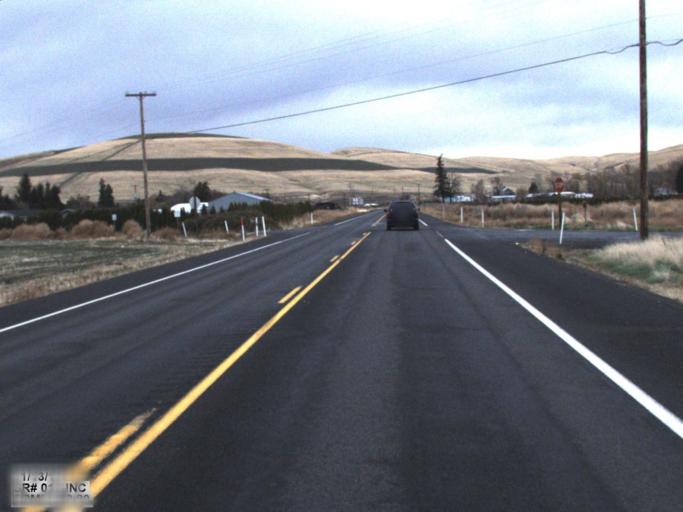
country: US
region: Washington
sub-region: Walla Walla County
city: Waitsburg
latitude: 46.2828
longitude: -118.1117
